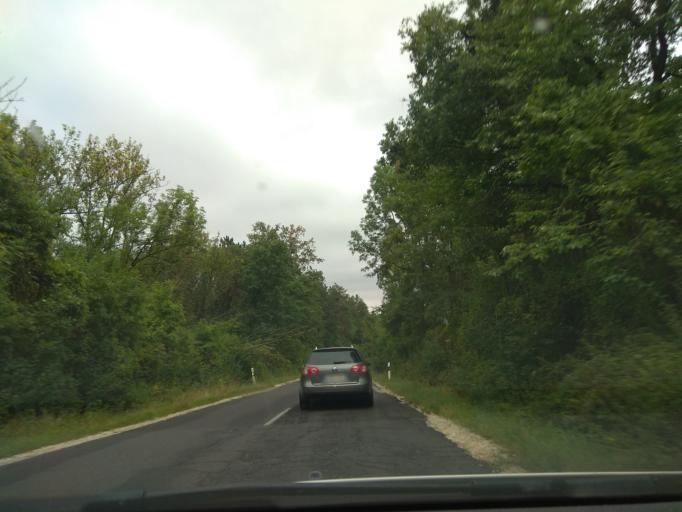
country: HU
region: Borsod-Abauj-Zemplen
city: Harsany
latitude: 48.0184
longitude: 20.7640
